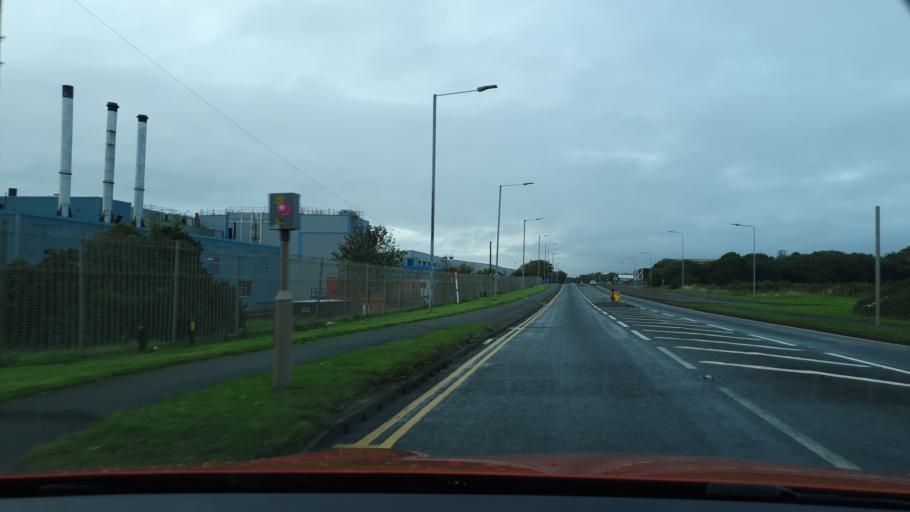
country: GB
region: England
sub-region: Cumbria
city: Barrow in Furness
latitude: 54.1415
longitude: -3.2321
